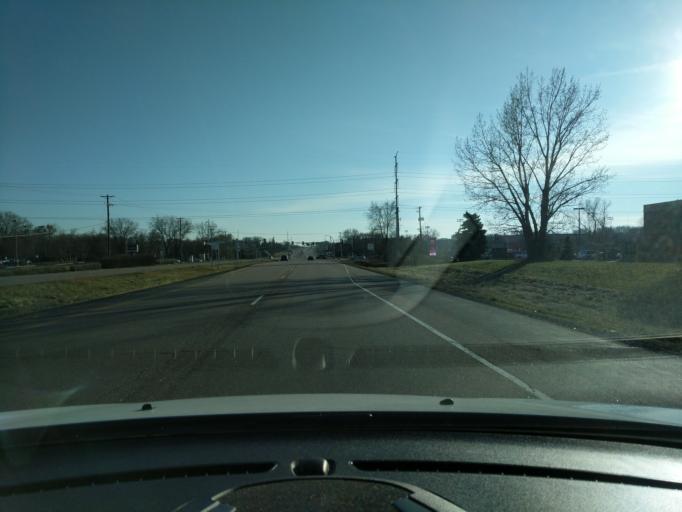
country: US
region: Minnesota
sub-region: Ramsey County
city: Roseville
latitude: 45.0227
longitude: -93.1672
